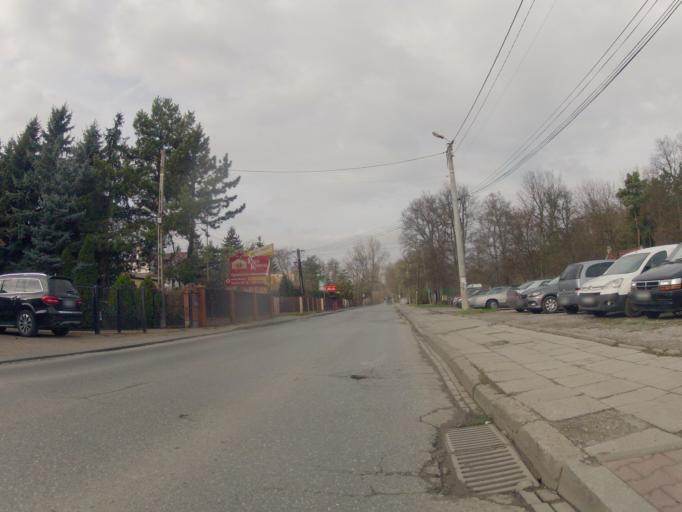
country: PL
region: Lesser Poland Voivodeship
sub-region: Powiat krakowski
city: Rzaska
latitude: 50.0865
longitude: 19.8423
